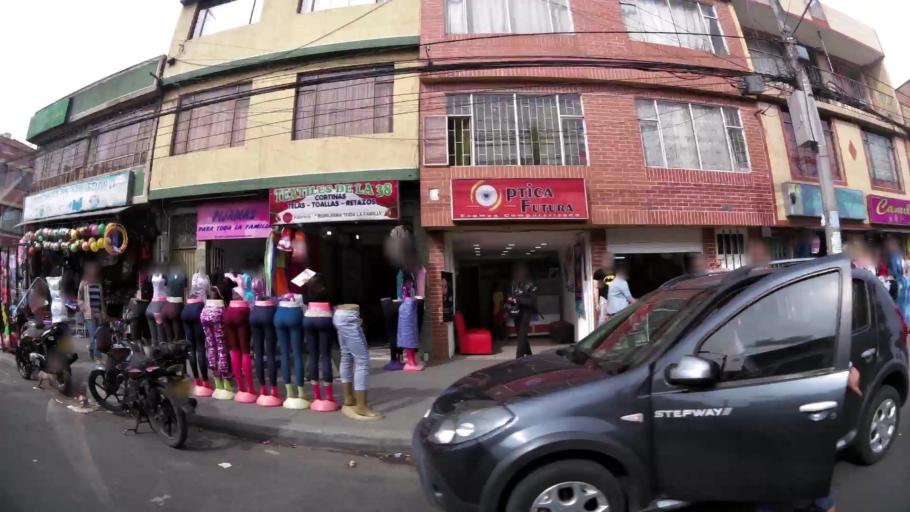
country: CO
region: Cundinamarca
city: Soacha
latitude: 4.6378
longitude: -74.1654
